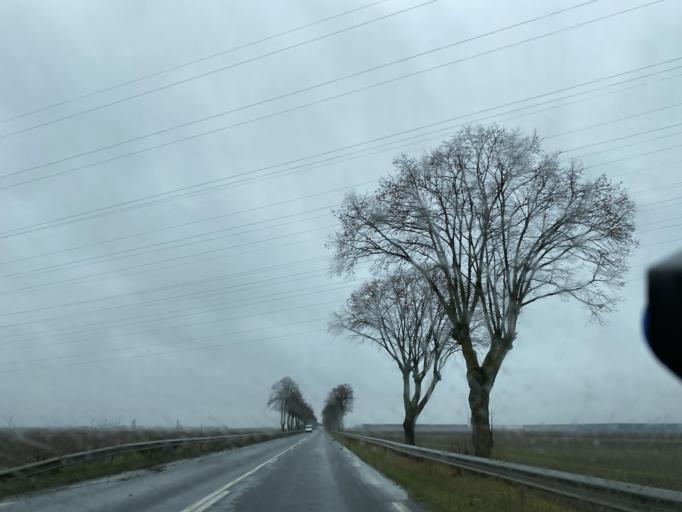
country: FR
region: Centre
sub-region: Departement du Loiret
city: Artenay
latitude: 48.1051
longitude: 1.8643
